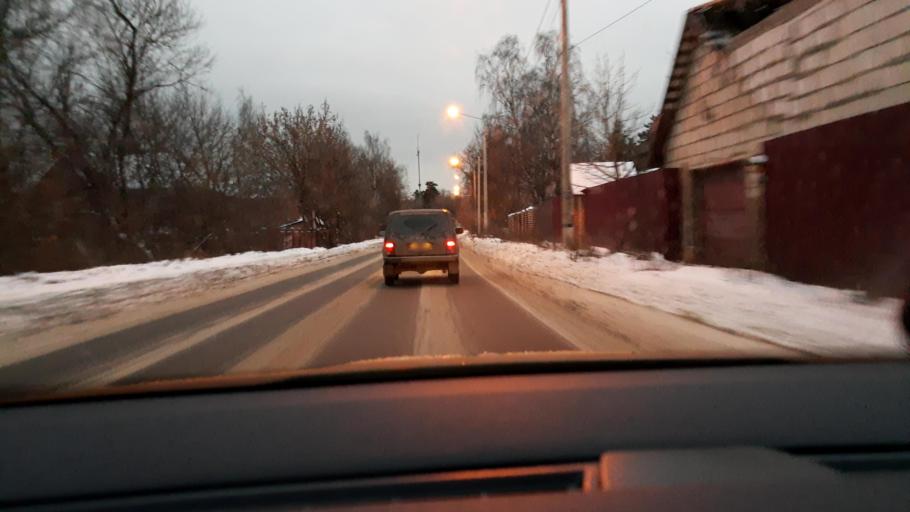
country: RU
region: Moskovskaya
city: Tomilino
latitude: 55.6454
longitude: 37.9526
